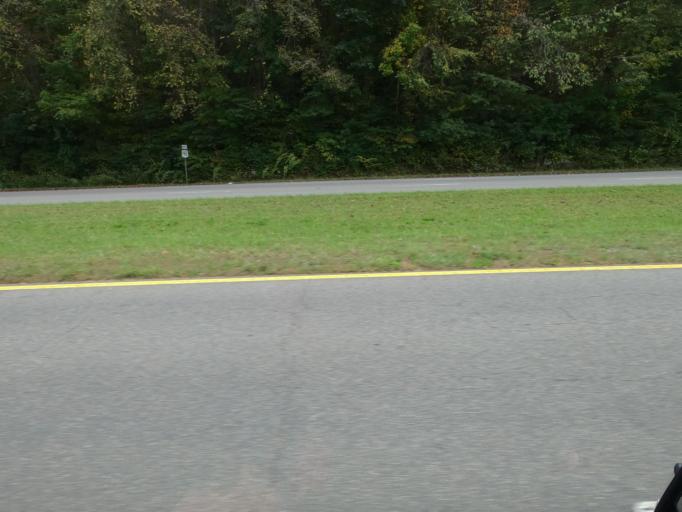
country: US
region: Tennessee
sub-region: Carter County
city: Elizabethton
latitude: 36.2619
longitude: -82.1859
